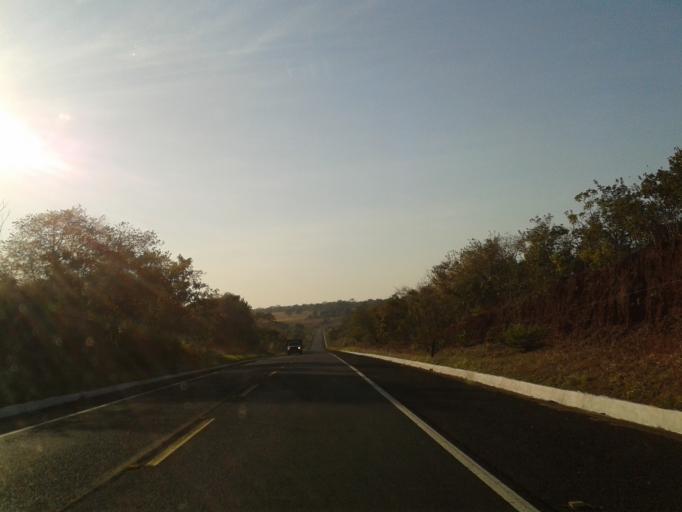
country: BR
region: Minas Gerais
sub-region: Santa Vitoria
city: Santa Vitoria
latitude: -19.1699
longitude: -50.0598
